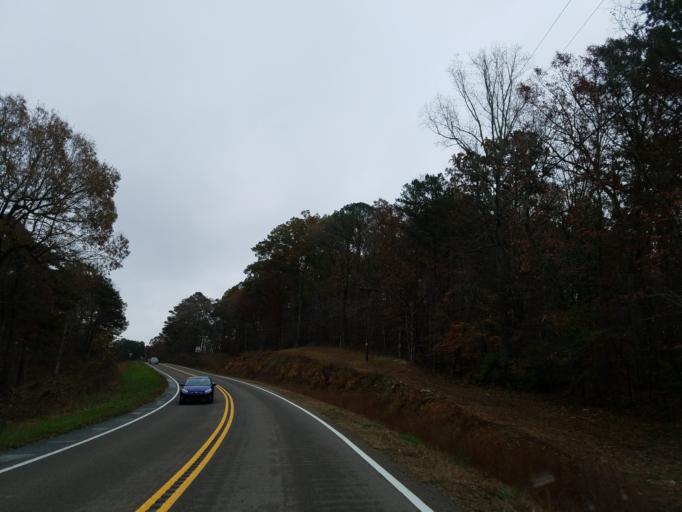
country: US
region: Georgia
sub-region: Cherokee County
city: Canton
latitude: 34.2638
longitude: -84.5912
